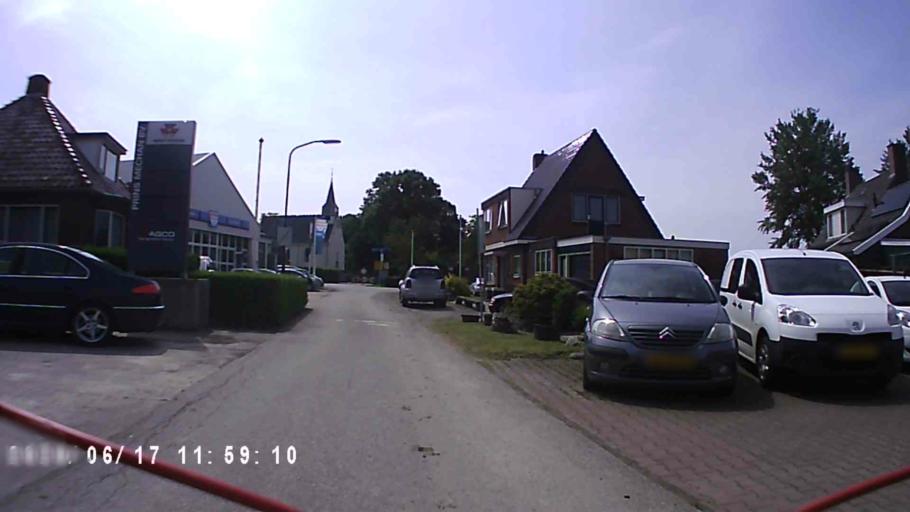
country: NL
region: Groningen
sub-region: Gemeente De Marne
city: Ulrum
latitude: 53.3426
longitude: 6.3289
